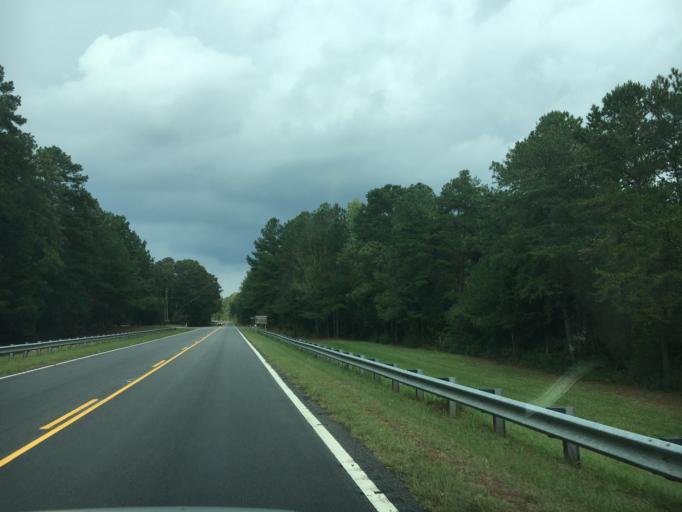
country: US
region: Georgia
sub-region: Hart County
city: Hartwell
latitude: 34.3743
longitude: -82.8130
